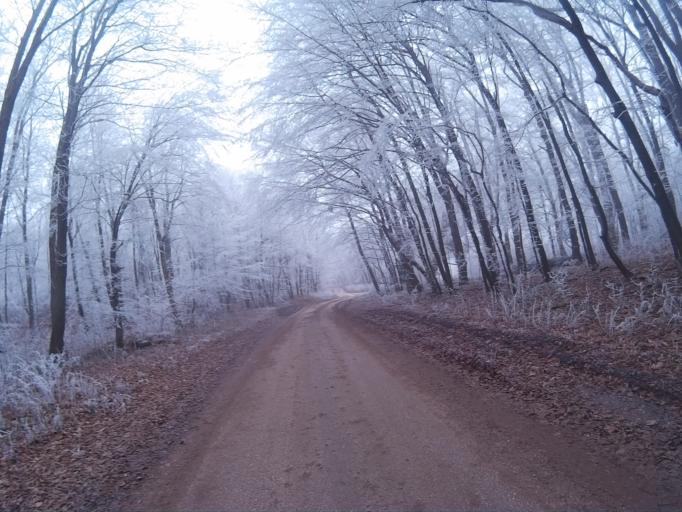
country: HU
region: Komarom-Esztergom
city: Oroszlany
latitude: 47.3986
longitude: 18.3120
